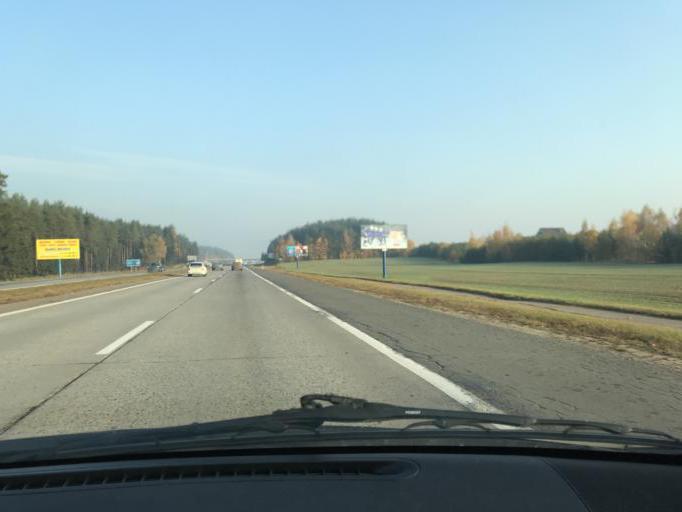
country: BY
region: Minsk
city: Borovlyany
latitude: 53.9971
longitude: 27.6572
